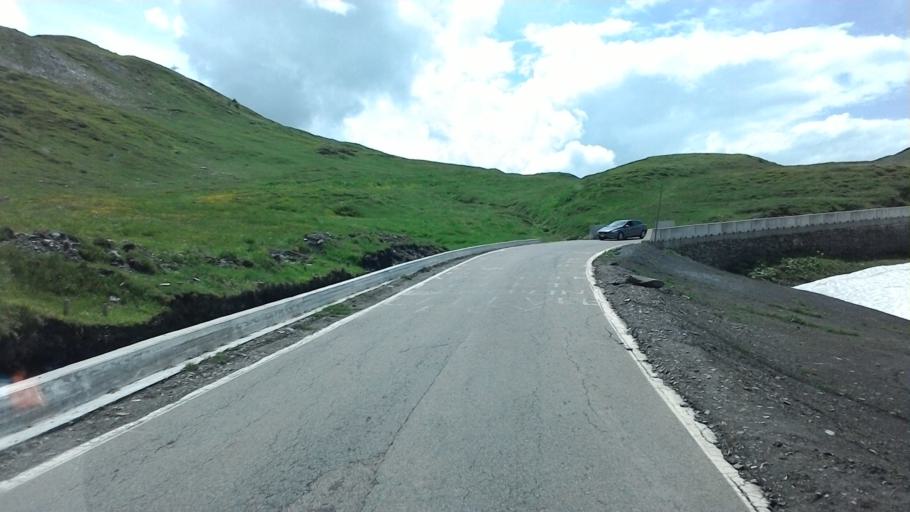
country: IT
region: Aosta Valley
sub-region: Valle d'Aosta
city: La Thuile
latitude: 45.6907
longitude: 6.8915
